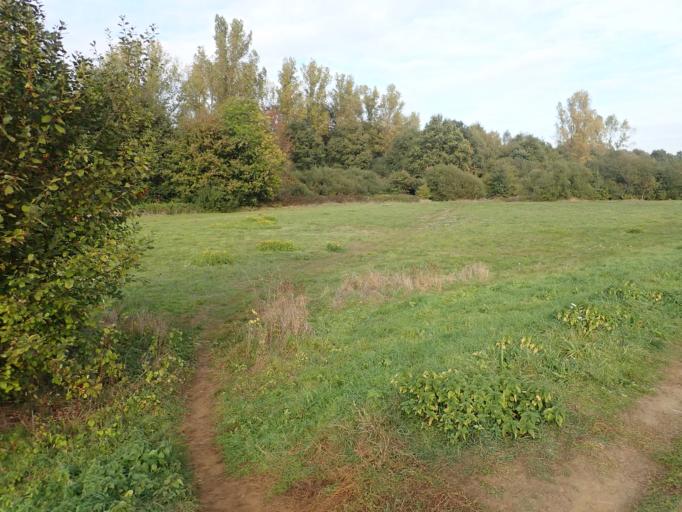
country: BE
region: Flanders
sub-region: Provincie Antwerpen
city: Berlaar
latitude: 51.1244
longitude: 4.7077
